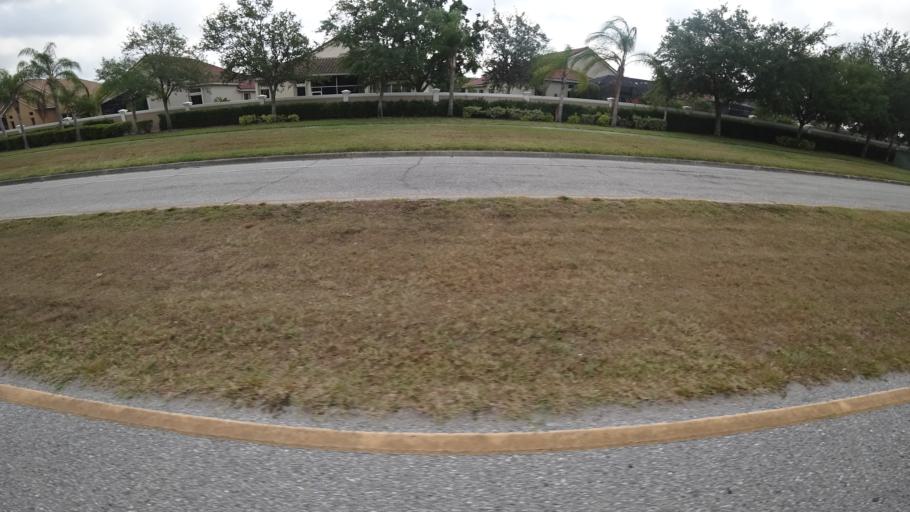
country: US
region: Florida
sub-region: Manatee County
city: Samoset
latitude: 27.4283
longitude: -82.5136
